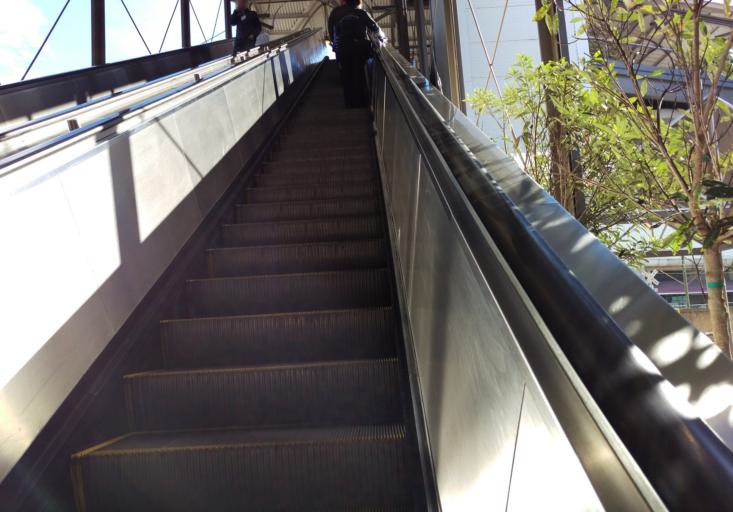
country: US
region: Louisiana
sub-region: Orleans Parish
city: New Orleans
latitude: 29.9441
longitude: -90.0629
